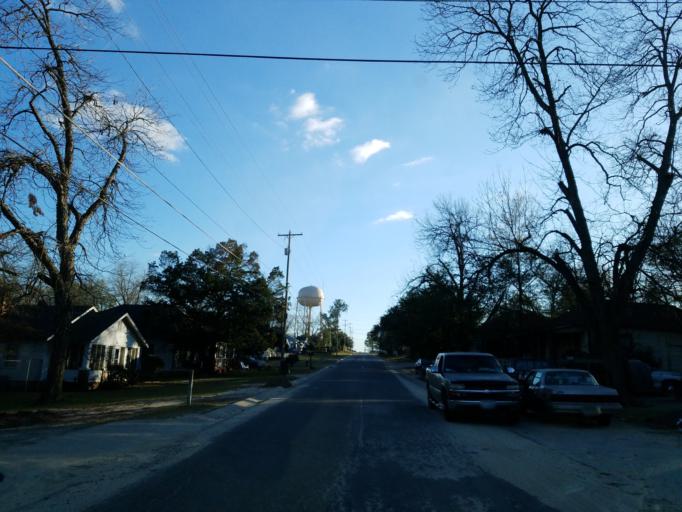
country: US
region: Georgia
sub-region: Crisp County
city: Cordele
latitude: 31.9587
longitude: -83.7863
